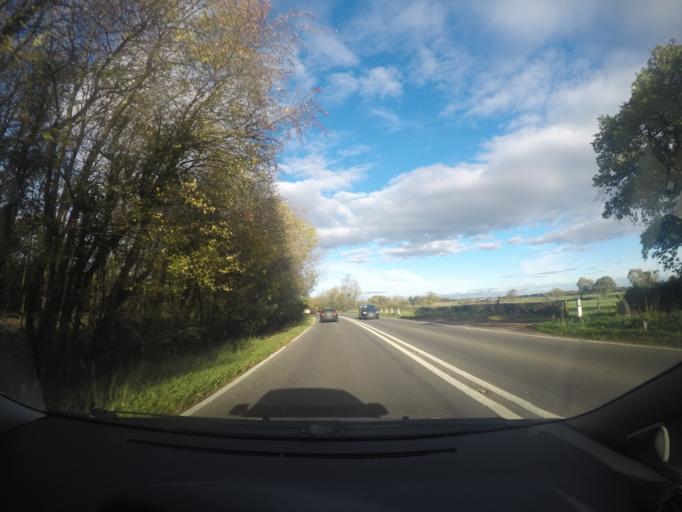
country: GB
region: England
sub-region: City and Borough of Leeds
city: Thorner
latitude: 53.8455
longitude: -1.4115
